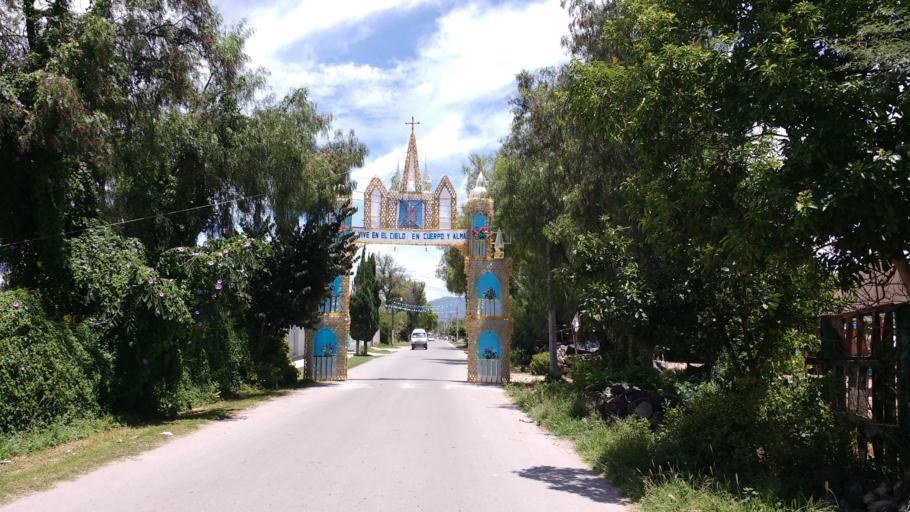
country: MX
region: Hidalgo
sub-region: Tezontepec de Aldama
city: Panuaya
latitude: 20.2269
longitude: -99.2544
